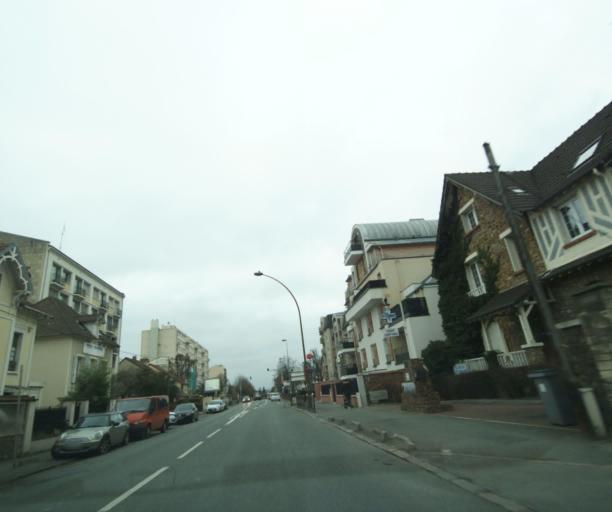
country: FR
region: Ile-de-France
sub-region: Departement des Yvelines
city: Poissy
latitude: 48.9302
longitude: 2.0470
